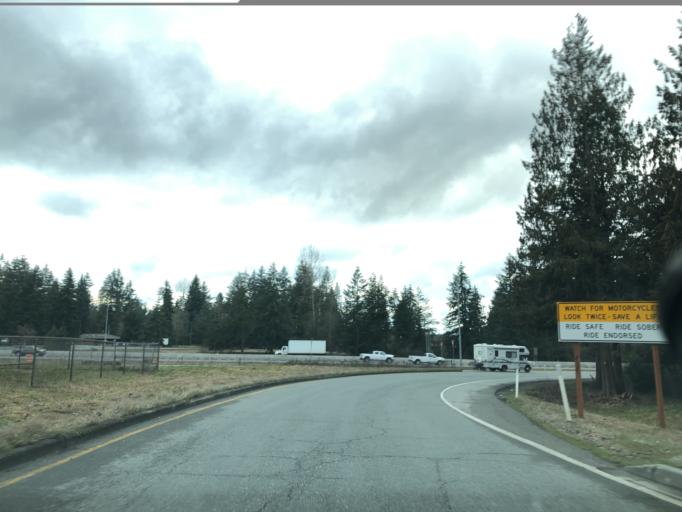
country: US
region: Washington
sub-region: Snohomish County
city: Smokey Point
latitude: 48.1705
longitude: -122.1902
